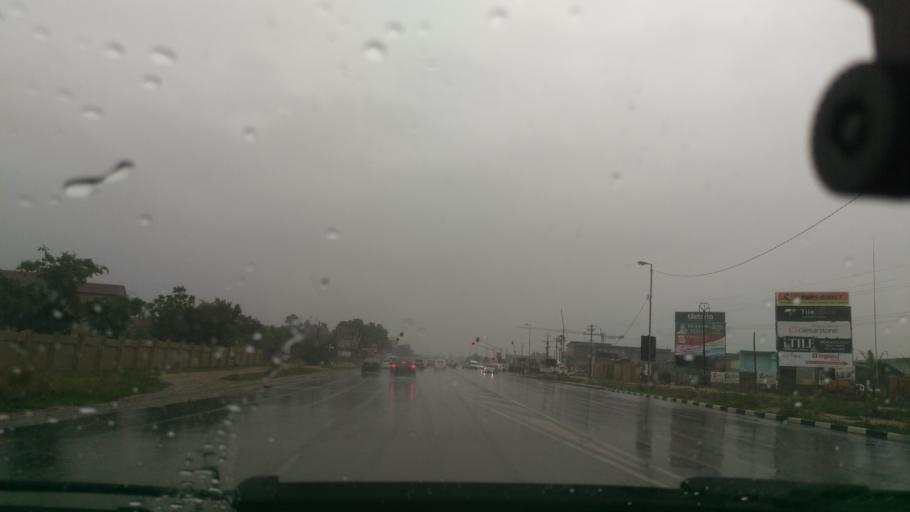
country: ZA
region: Gauteng
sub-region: City of Johannesburg Metropolitan Municipality
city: Diepsloot
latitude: -26.0387
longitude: 27.9598
